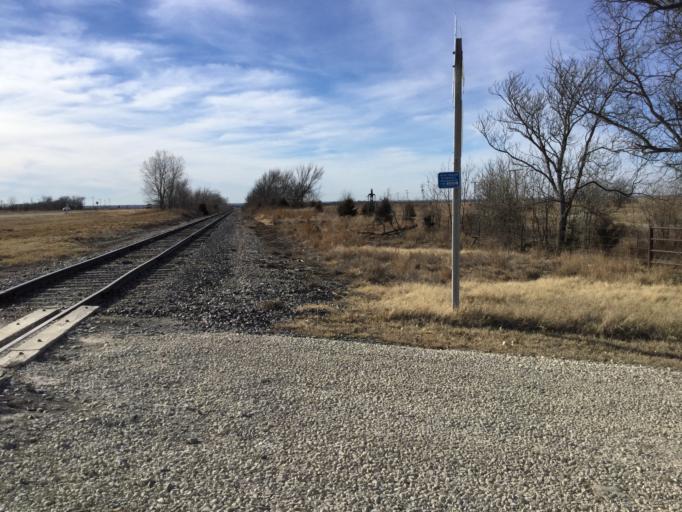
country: US
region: Kansas
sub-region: Butler County
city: Towanda
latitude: 37.8127
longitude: -96.9530
